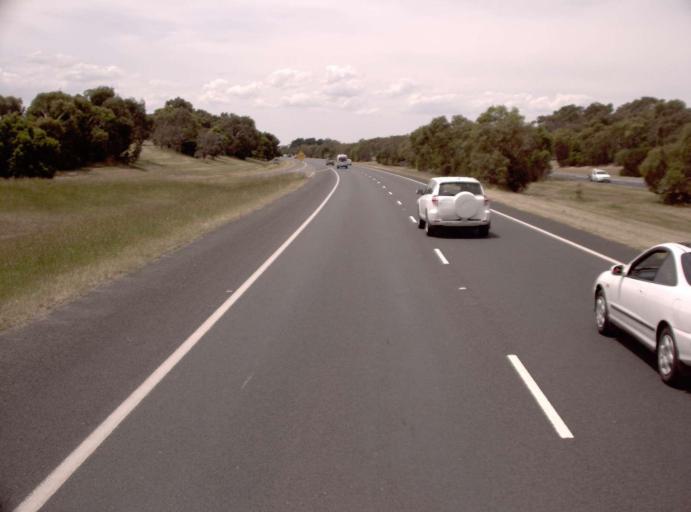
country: AU
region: Victoria
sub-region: Mornington Peninsula
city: Mount Martha
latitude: -38.2994
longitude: 145.0346
